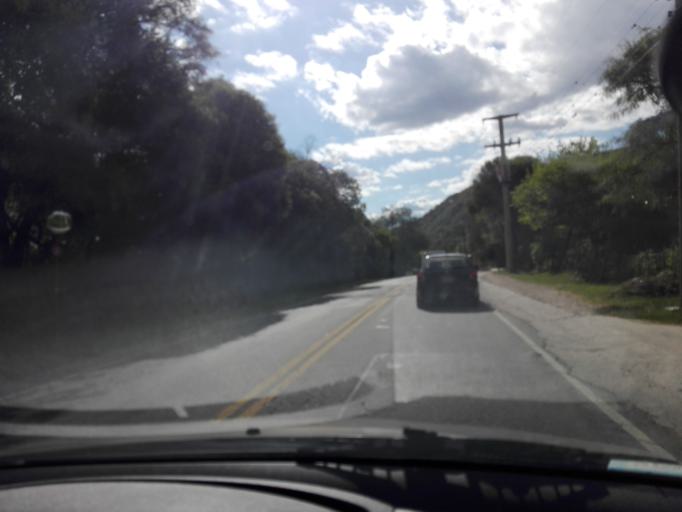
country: AR
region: Cordoba
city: Villa Las Rosas
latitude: -31.9091
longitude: -64.9949
